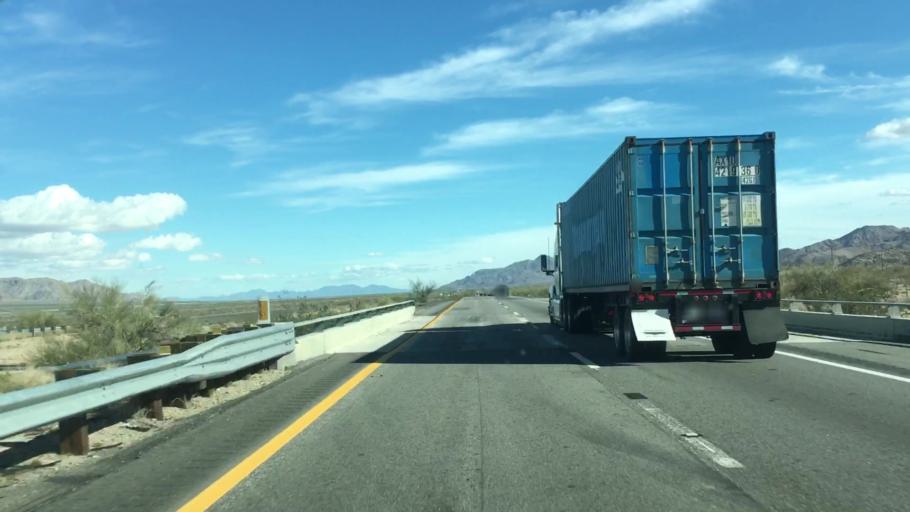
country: US
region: California
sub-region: Imperial County
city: Niland
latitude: 33.6692
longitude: -115.6394
